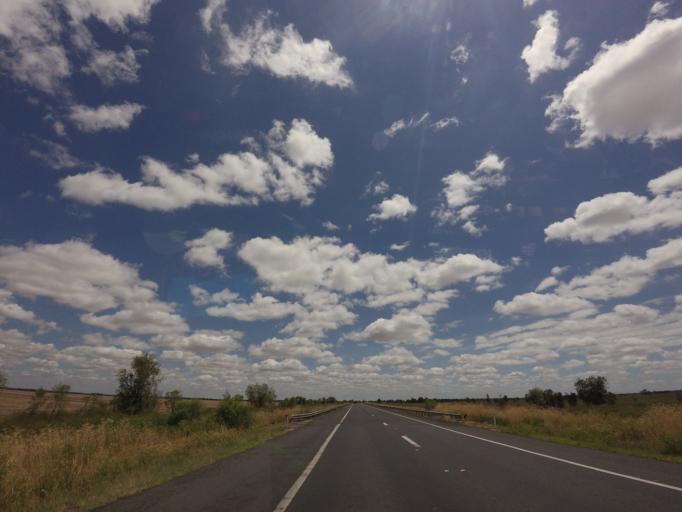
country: AU
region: New South Wales
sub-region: Moree Plains
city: Moree
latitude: -29.0256
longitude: 150.0590
